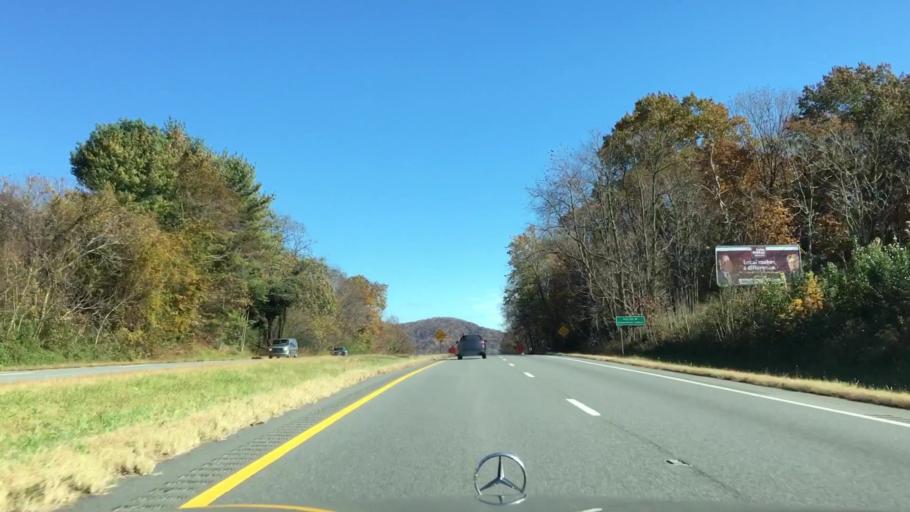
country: US
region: Virginia
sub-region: Albemarle County
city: Crozet
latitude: 37.9682
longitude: -78.6382
